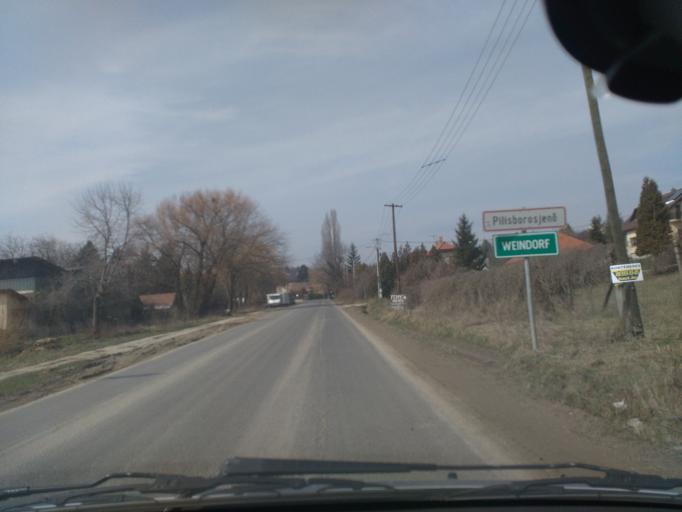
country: HU
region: Pest
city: Pilisborosjeno
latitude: 47.6039
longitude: 18.9976
